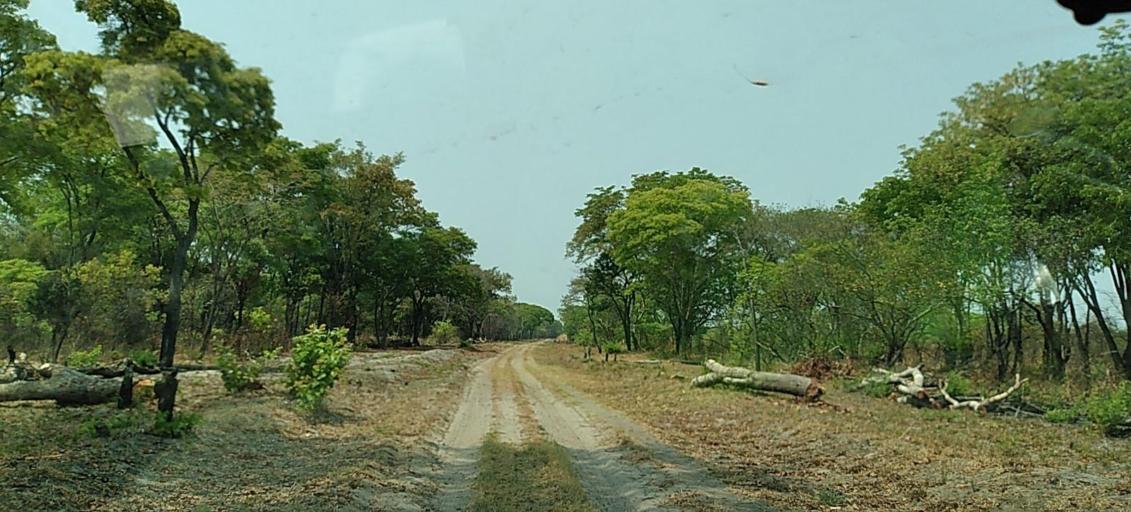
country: ZM
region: Western
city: Lukulu
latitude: -13.9510
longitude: 23.2241
